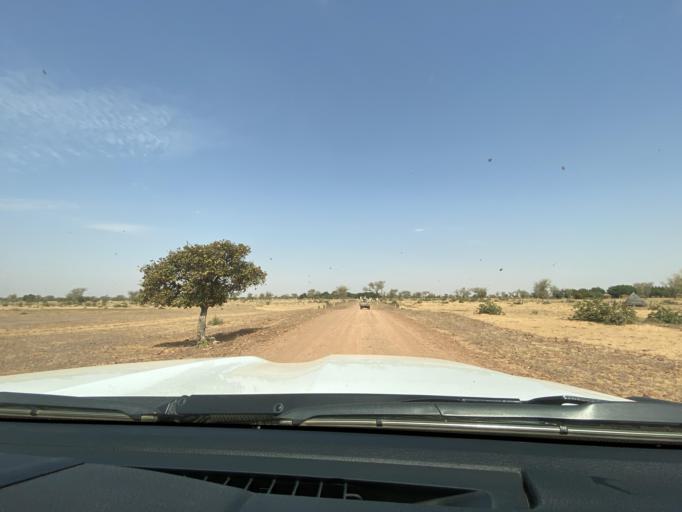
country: NE
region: Dosso
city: Birnin Gaoure
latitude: 13.2383
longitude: 2.8672
